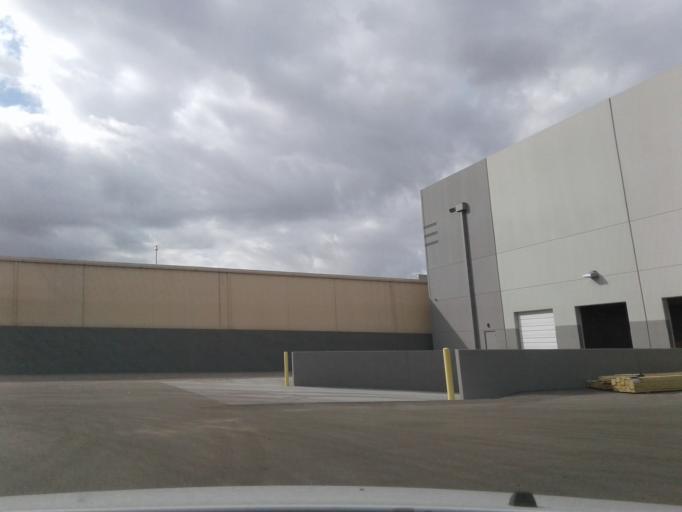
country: US
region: Arizona
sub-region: Maricopa County
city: Phoenix
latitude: 33.4305
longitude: -112.0847
